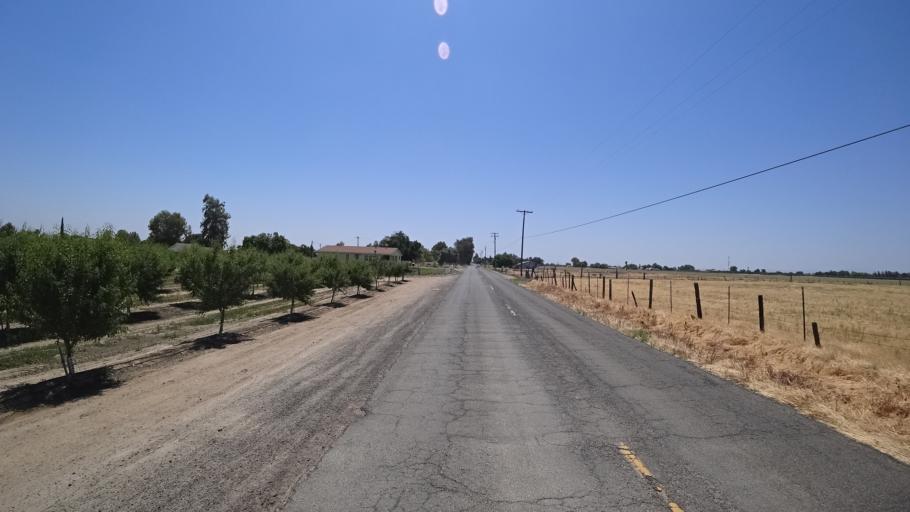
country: US
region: California
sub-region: Kings County
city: Lemoore
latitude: 36.2769
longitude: -119.7629
